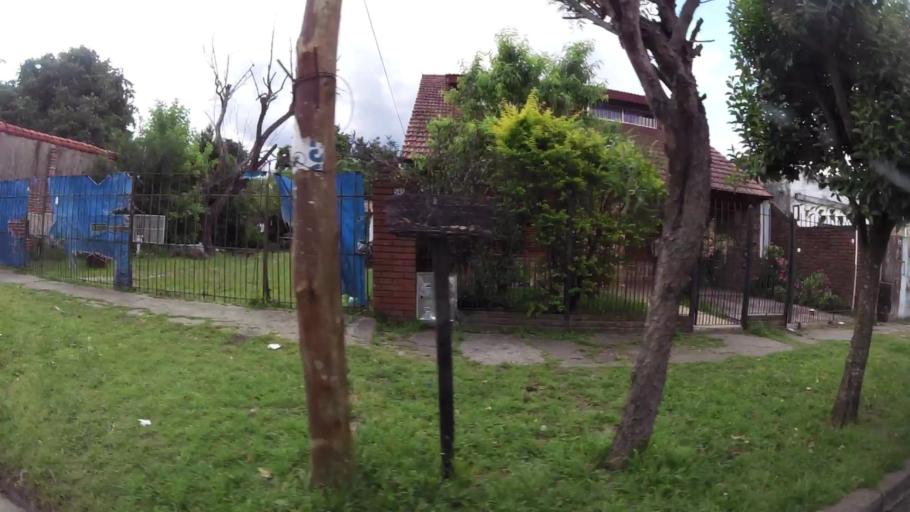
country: AR
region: Buenos Aires
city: Ituzaingo
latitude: -34.6343
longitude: -58.6793
